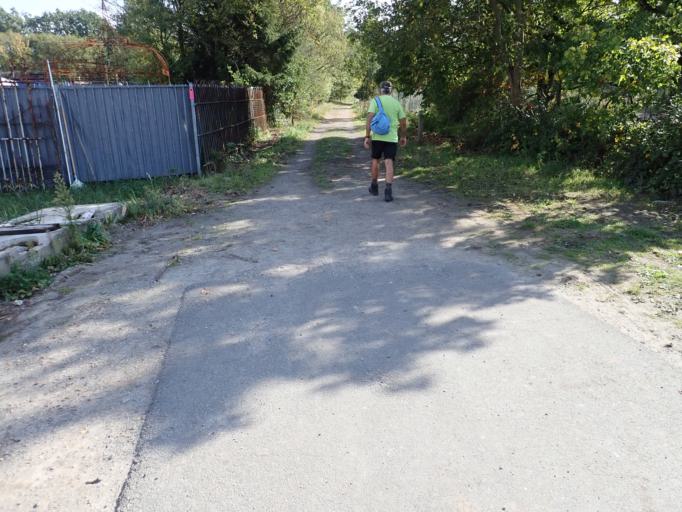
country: NL
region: Zeeland
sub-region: Gemeente Hulst
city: Hulst
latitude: 51.2490
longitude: 4.0742
